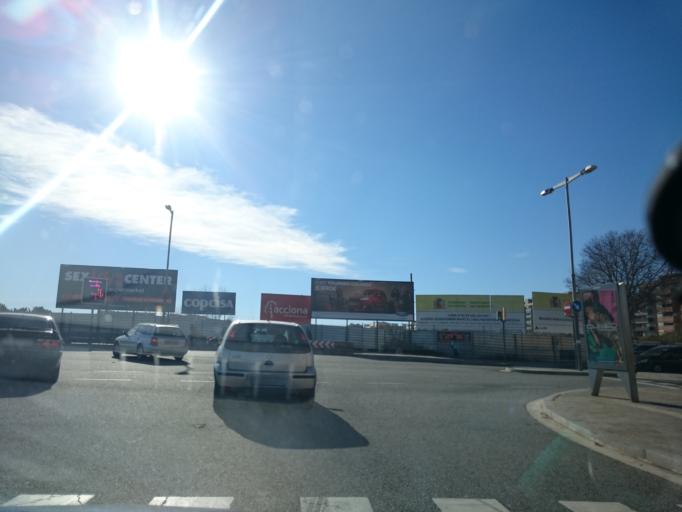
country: ES
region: Catalonia
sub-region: Provincia de Barcelona
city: Sant Andreu de Palomar
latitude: 41.4426
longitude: 2.1944
